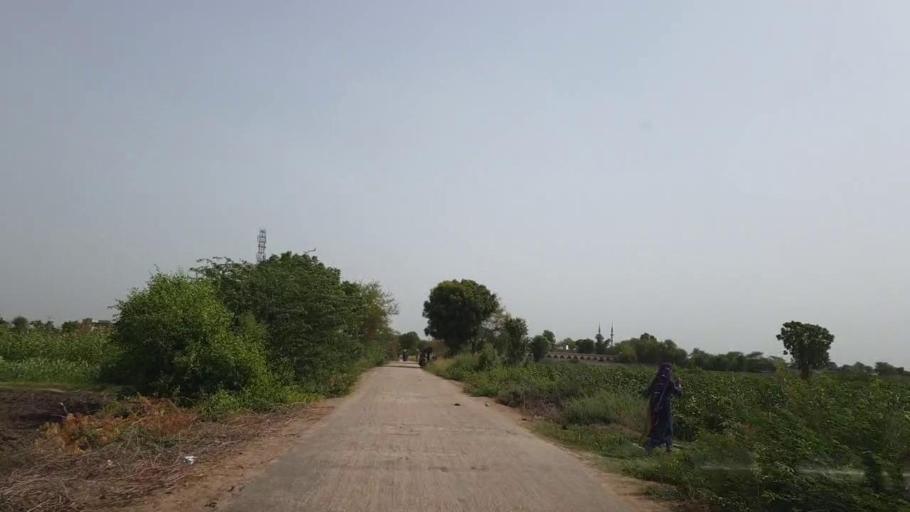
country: PK
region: Sindh
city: Sakrand
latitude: 26.1135
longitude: 68.3972
